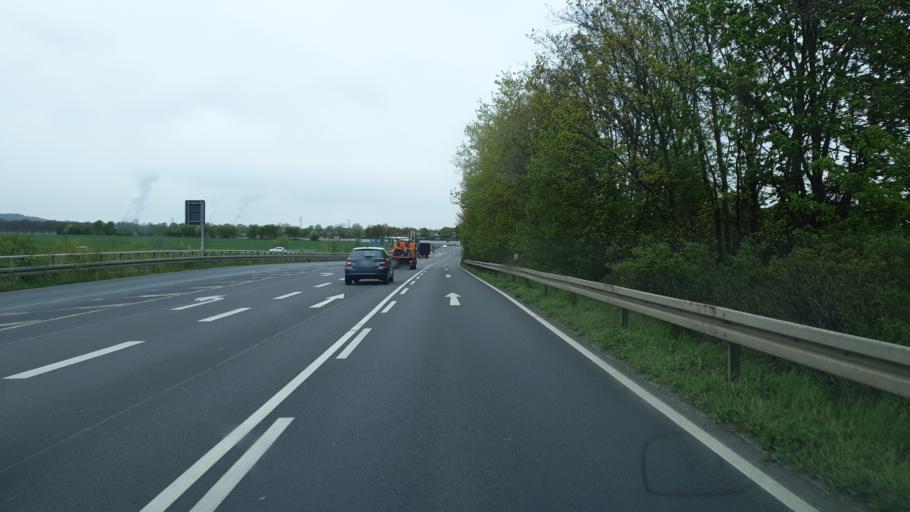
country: DE
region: North Rhine-Westphalia
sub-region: Regierungsbezirk Koln
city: Frechen
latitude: 50.9310
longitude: 6.8189
